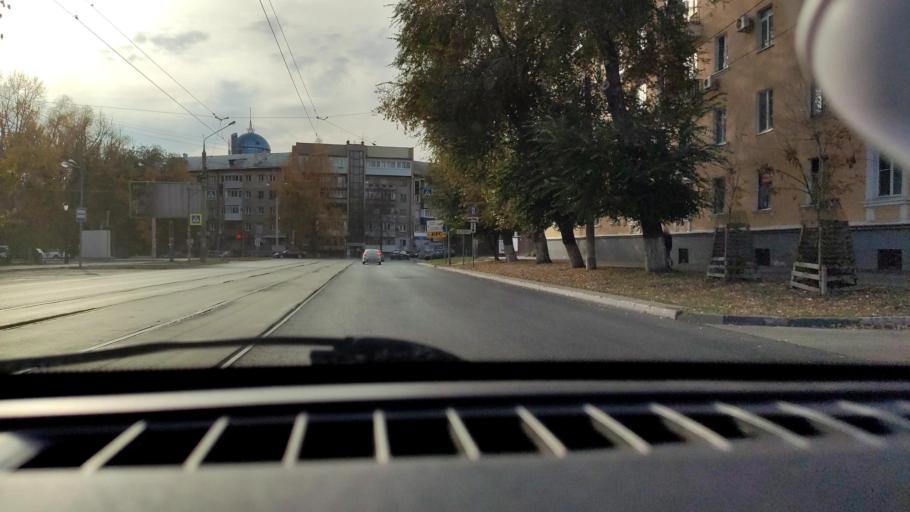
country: RU
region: Samara
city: Samara
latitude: 53.1882
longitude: 50.1265
